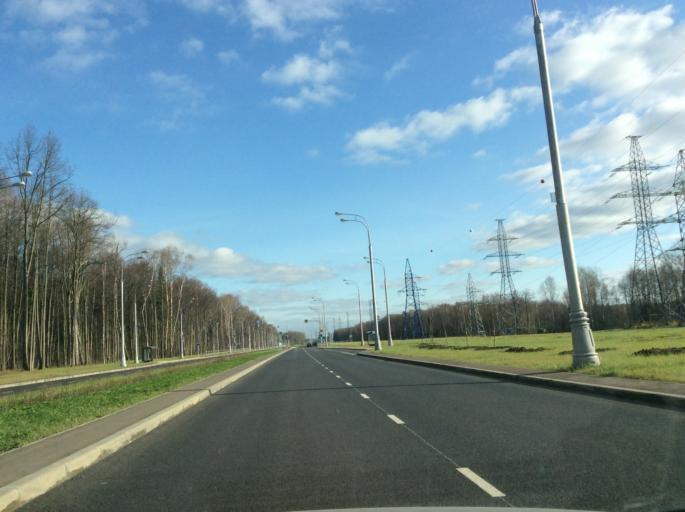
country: RU
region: Moskovskaya
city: Vatutinki
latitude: 55.4833
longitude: 37.3523
